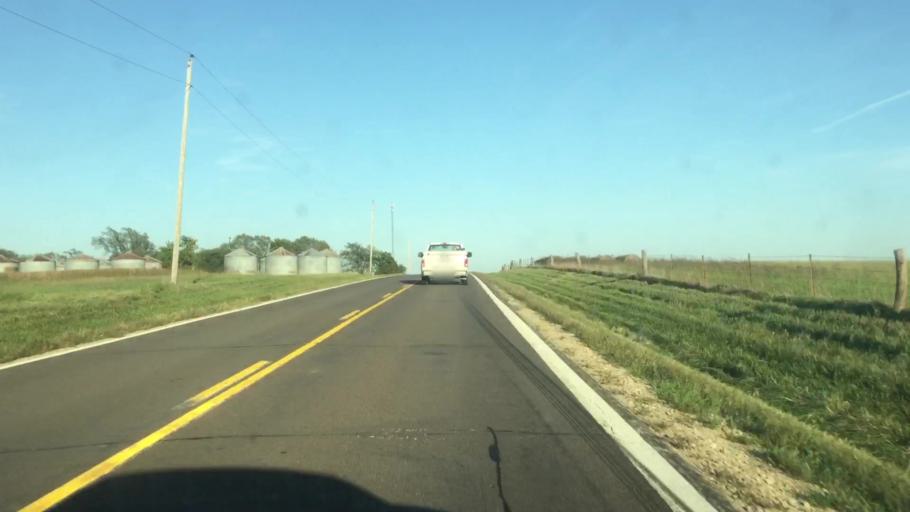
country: US
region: Kansas
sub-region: Brown County
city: Horton
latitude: 39.5514
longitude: -95.4364
